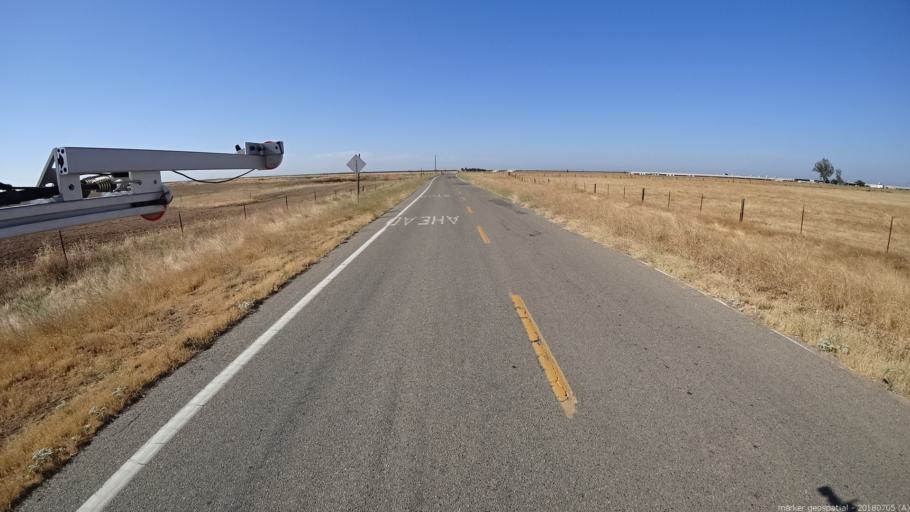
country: US
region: California
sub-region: Madera County
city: Madera Acres
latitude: 37.1247
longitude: -120.0746
